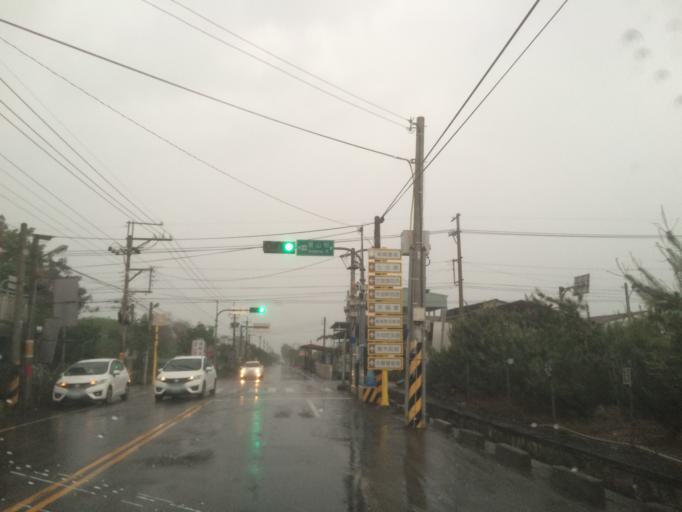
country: TW
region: Taiwan
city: Fengyuan
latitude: 24.2191
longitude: 120.8033
